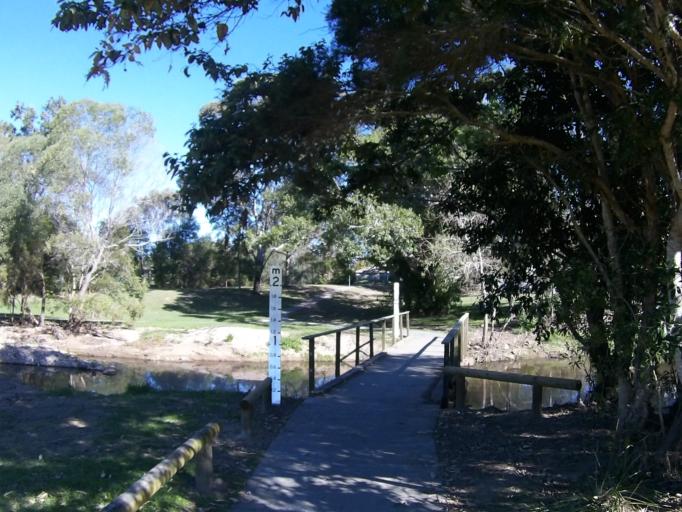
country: AU
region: Queensland
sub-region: Logan
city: Windaroo
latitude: -27.7380
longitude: 153.1933
